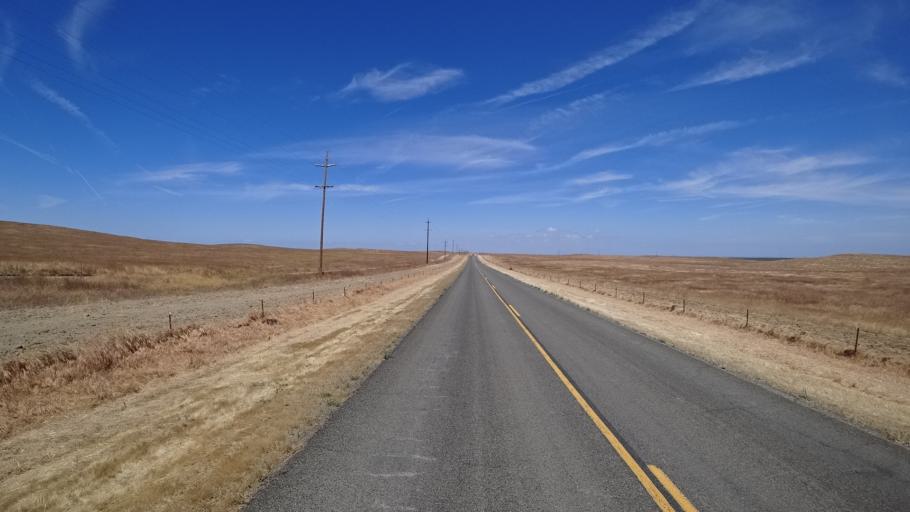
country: US
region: California
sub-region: Kings County
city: Kettleman City
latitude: 35.8705
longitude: -119.9153
